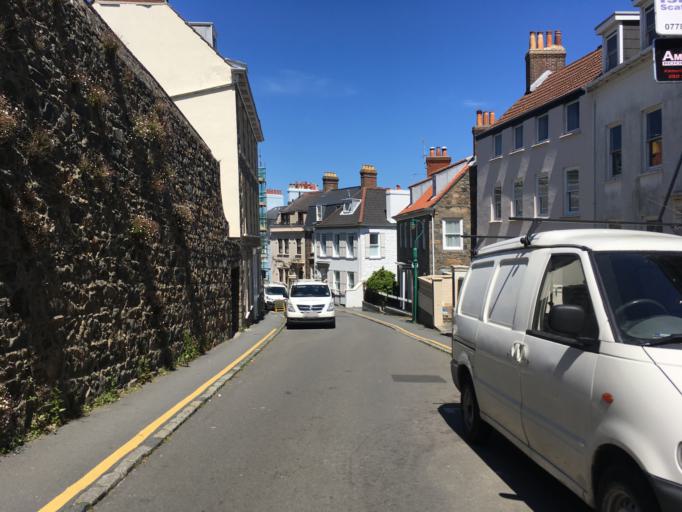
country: GG
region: St Peter Port
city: Saint Peter Port
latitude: 49.4515
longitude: -2.5377
